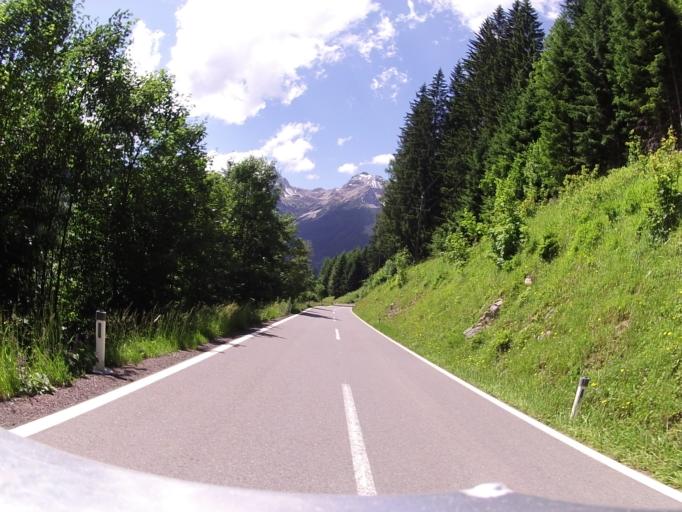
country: AT
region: Tyrol
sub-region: Politischer Bezirk Reutte
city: Elmen
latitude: 47.3177
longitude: 10.5539
